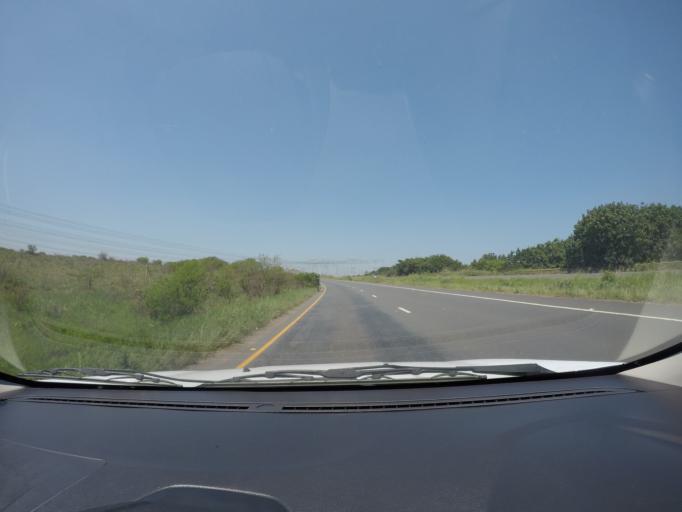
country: ZA
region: KwaZulu-Natal
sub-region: uThungulu District Municipality
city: Richards Bay
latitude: -28.7796
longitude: 32.0003
